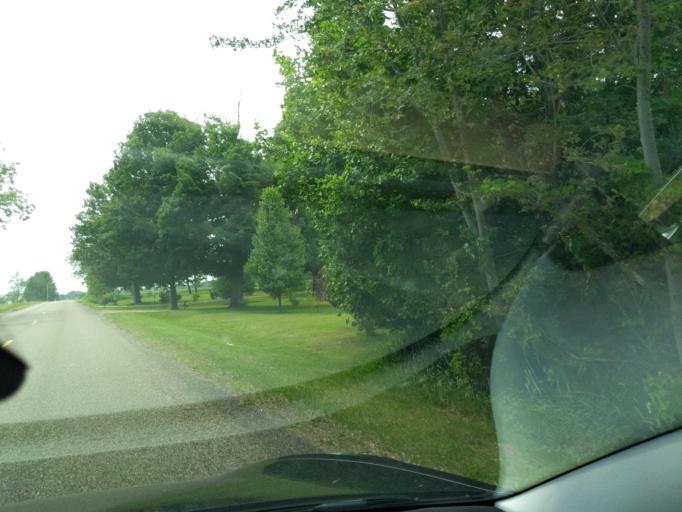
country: US
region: Michigan
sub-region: Ionia County
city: Lake Odessa
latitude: 42.7125
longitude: -85.0502
